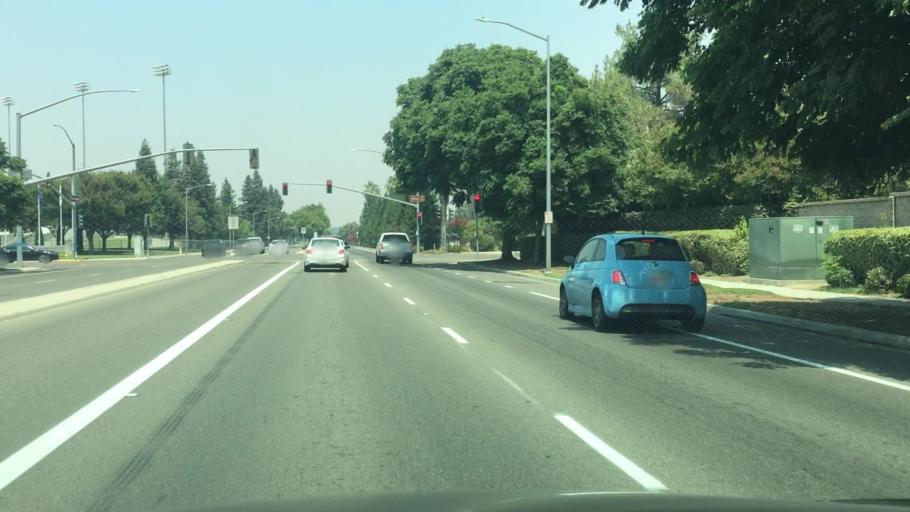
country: US
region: California
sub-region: Fresno County
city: Clovis
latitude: 36.8515
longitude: -119.7110
